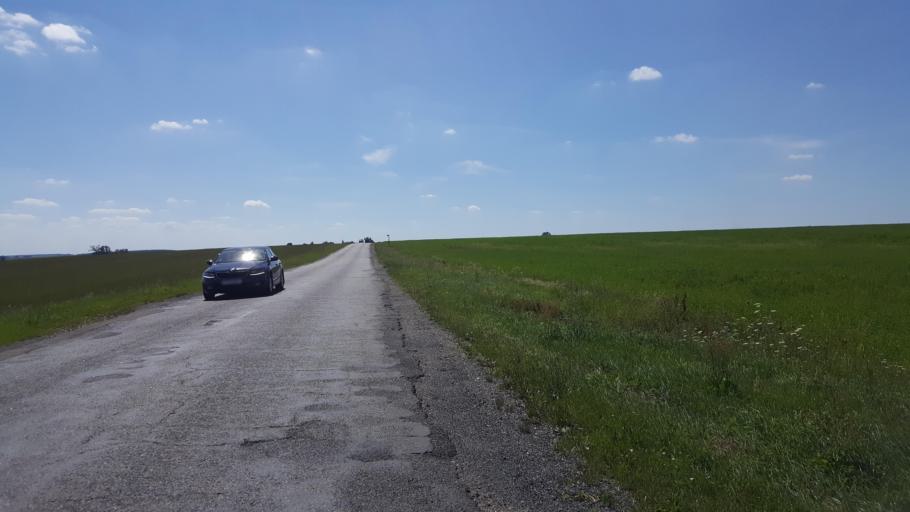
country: BY
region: Brest
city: Charnawchytsy
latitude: 52.3086
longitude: 23.6073
